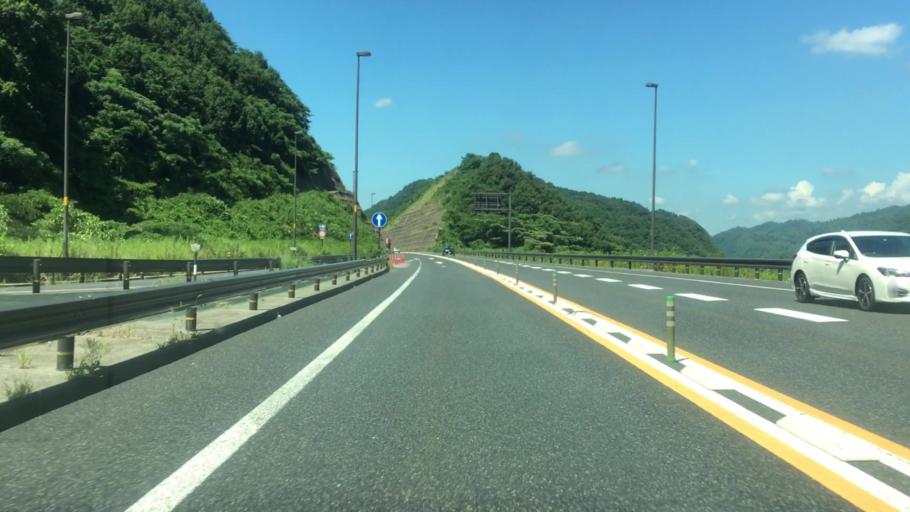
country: JP
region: Tottori
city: Tottori
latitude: 35.3567
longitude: 134.1974
